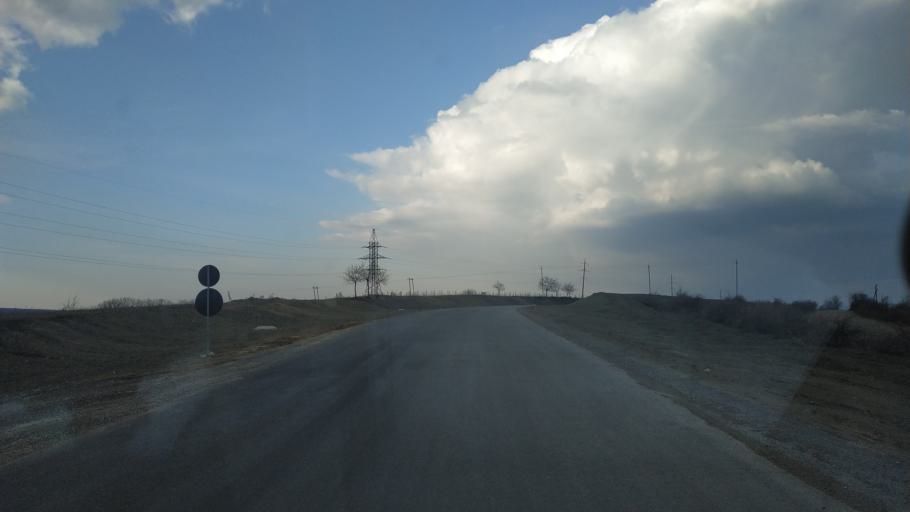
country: MD
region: Anenii Noi
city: Anenii Noi
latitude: 46.9921
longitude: 29.2839
